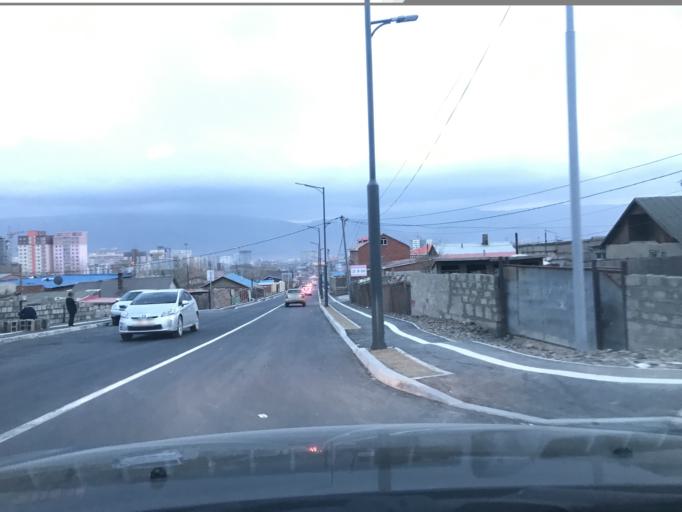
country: MN
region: Ulaanbaatar
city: Ulaanbaatar
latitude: 47.9282
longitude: 106.9735
